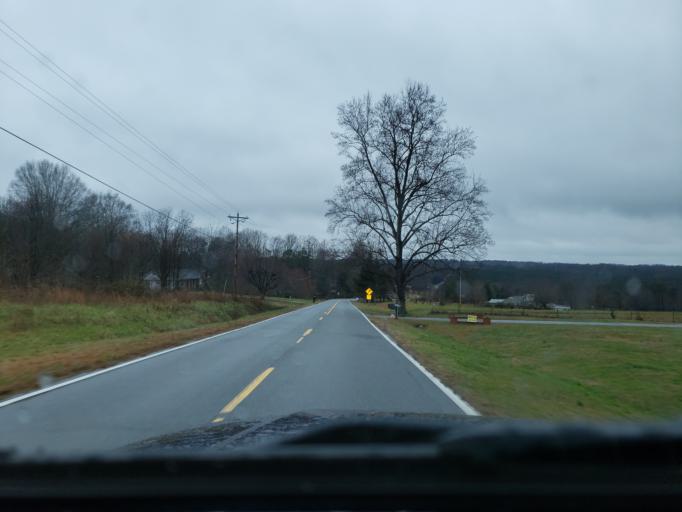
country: US
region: North Carolina
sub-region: Cleveland County
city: White Plains
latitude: 35.1774
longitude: -81.3667
